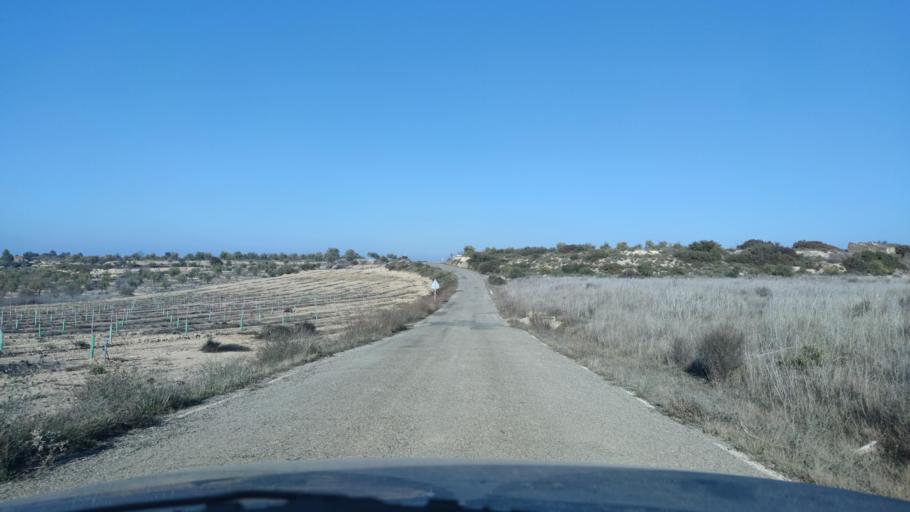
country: ES
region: Catalonia
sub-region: Provincia de Lleida
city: Torrebesses
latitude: 41.4089
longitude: 0.5694
